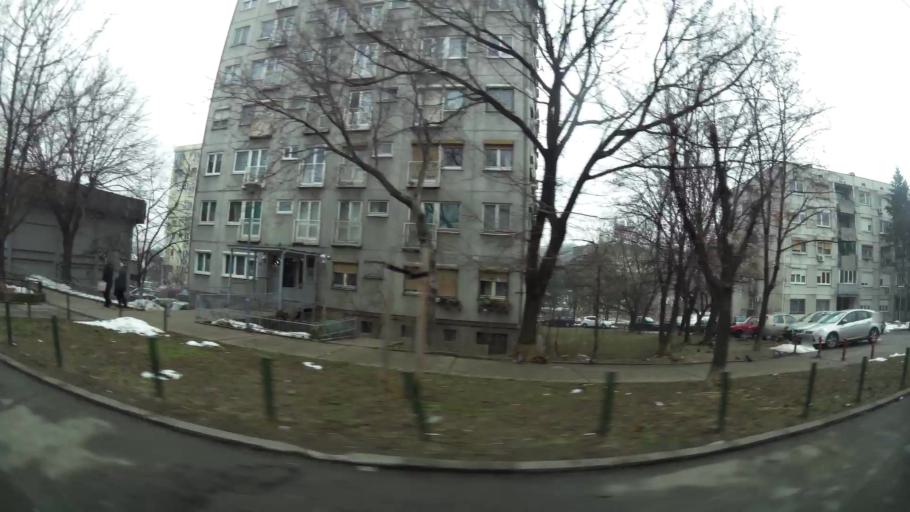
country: RS
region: Central Serbia
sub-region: Belgrade
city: Vozdovac
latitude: 44.7778
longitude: 20.4805
